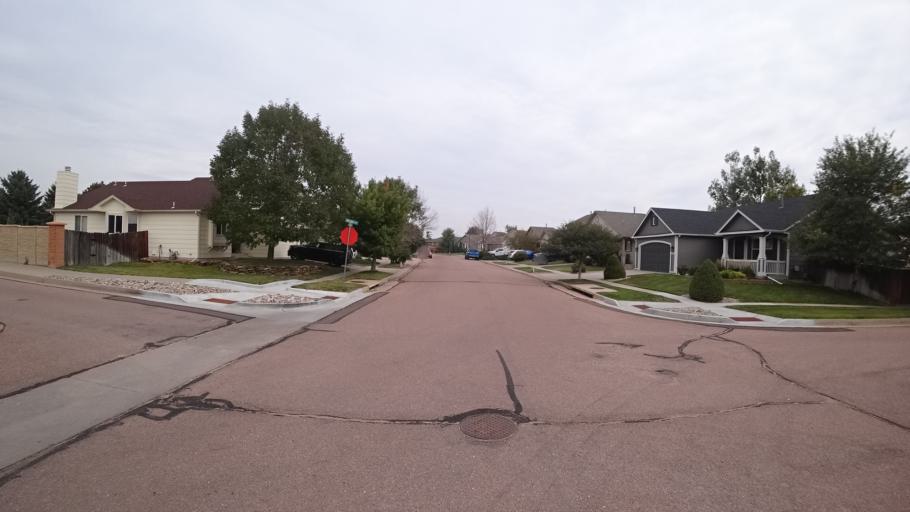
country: US
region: Colorado
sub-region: El Paso County
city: Cimarron Hills
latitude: 38.9155
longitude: -104.6924
